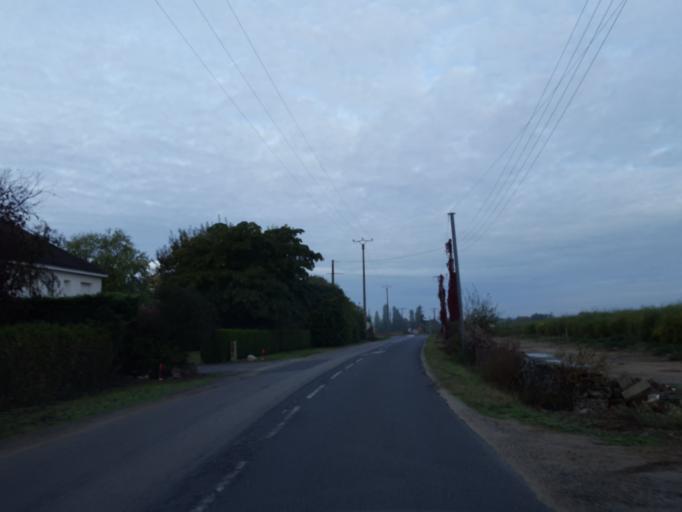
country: FR
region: Pays de la Loire
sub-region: Departement de la Loire-Atlantique
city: Saint-Julien-de-Concelles
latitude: 47.2464
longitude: -1.3994
